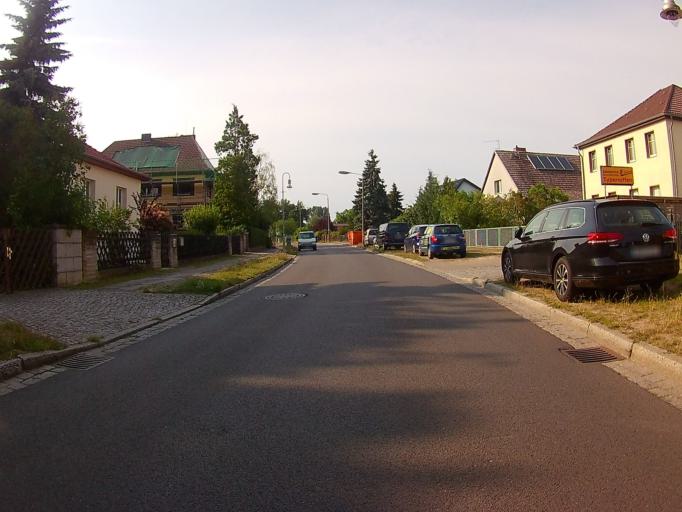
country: DE
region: Berlin
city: Kopenick Bezirk
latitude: 52.4647
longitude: 13.5709
